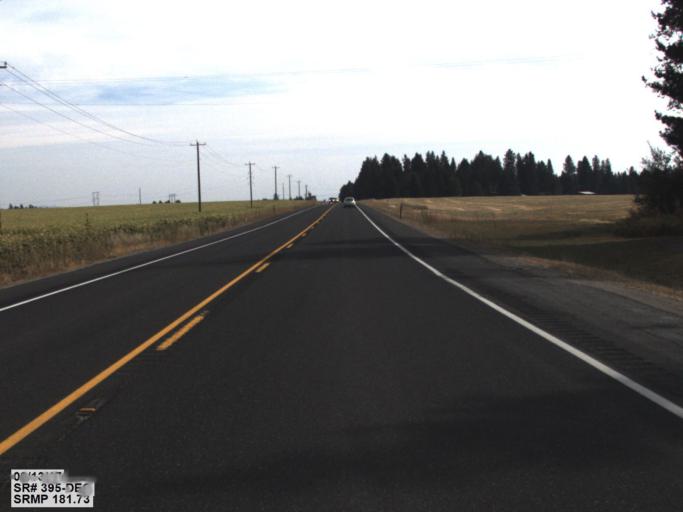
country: US
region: Washington
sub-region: Spokane County
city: Deer Park
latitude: 47.9673
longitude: -117.5070
